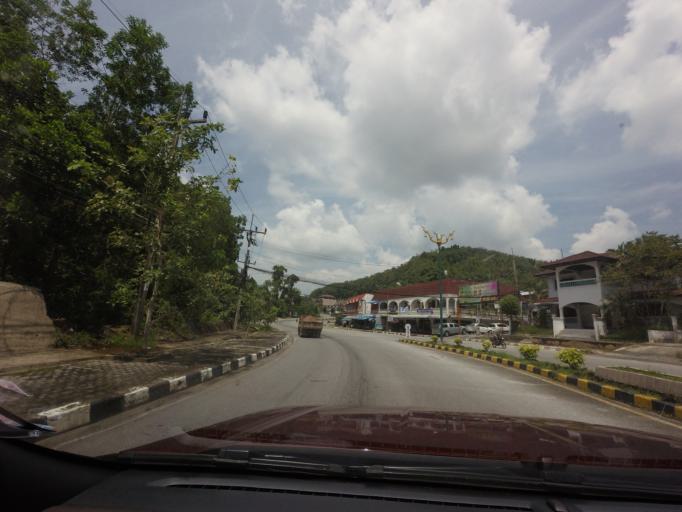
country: TH
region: Yala
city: Betong
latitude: 5.7735
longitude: 101.0599
